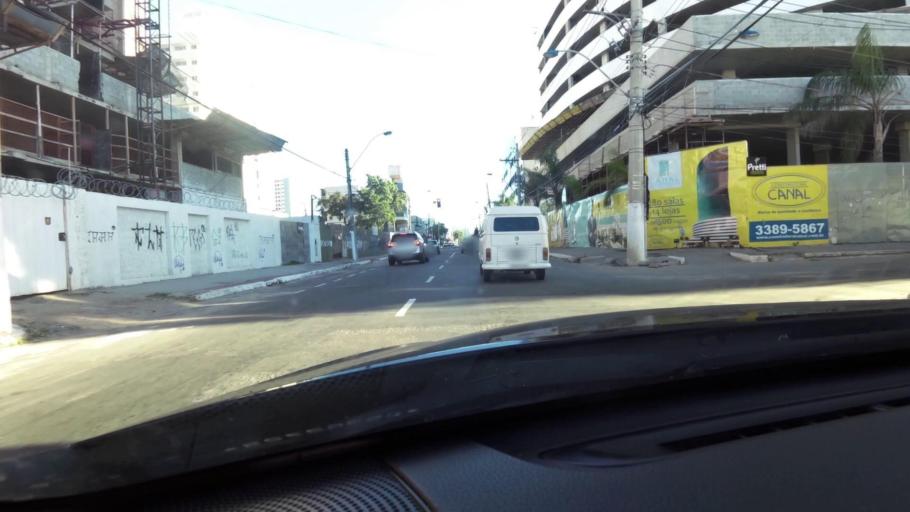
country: BR
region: Espirito Santo
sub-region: Vila Velha
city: Vila Velha
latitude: -20.3585
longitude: -40.2977
